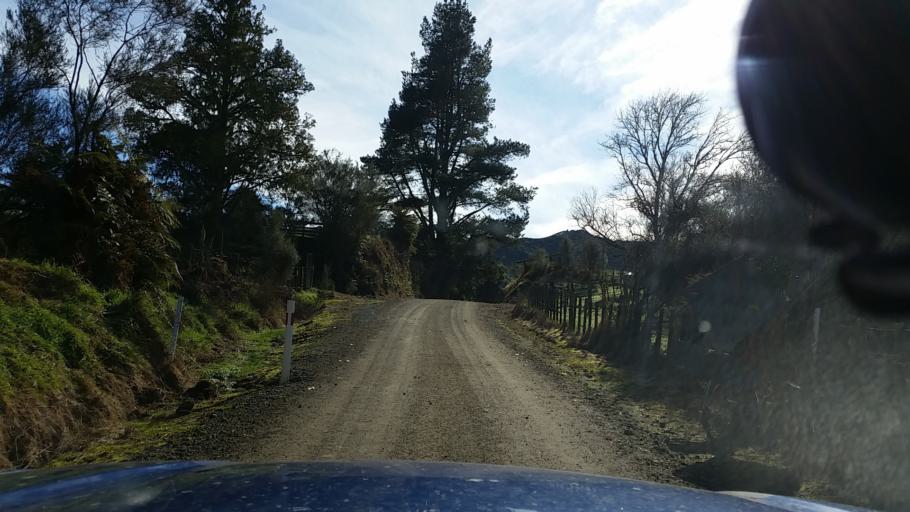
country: NZ
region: Taranaki
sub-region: New Plymouth District
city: Waitara
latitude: -39.0557
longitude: 174.7731
